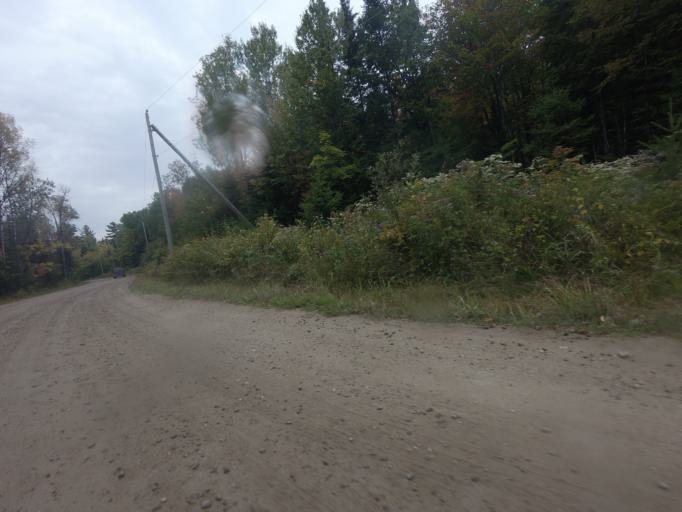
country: CA
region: Quebec
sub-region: Outaouais
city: Maniwaki
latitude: 46.0390
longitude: -75.9378
